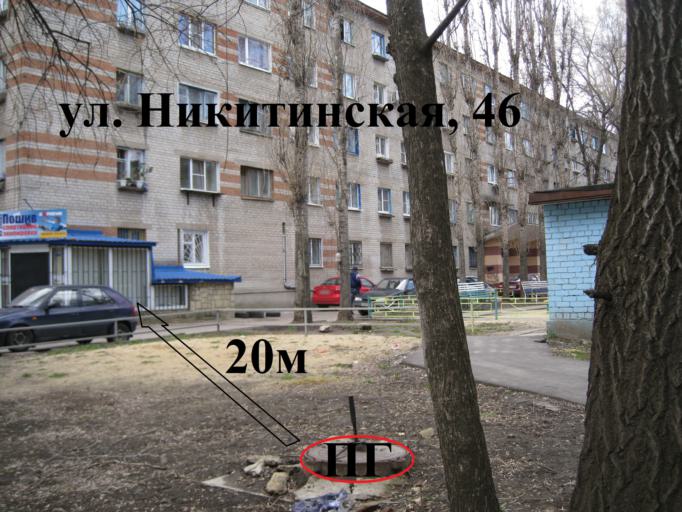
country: RU
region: Voronezj
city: Voronezh
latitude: 51.6639
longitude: 39.1913
